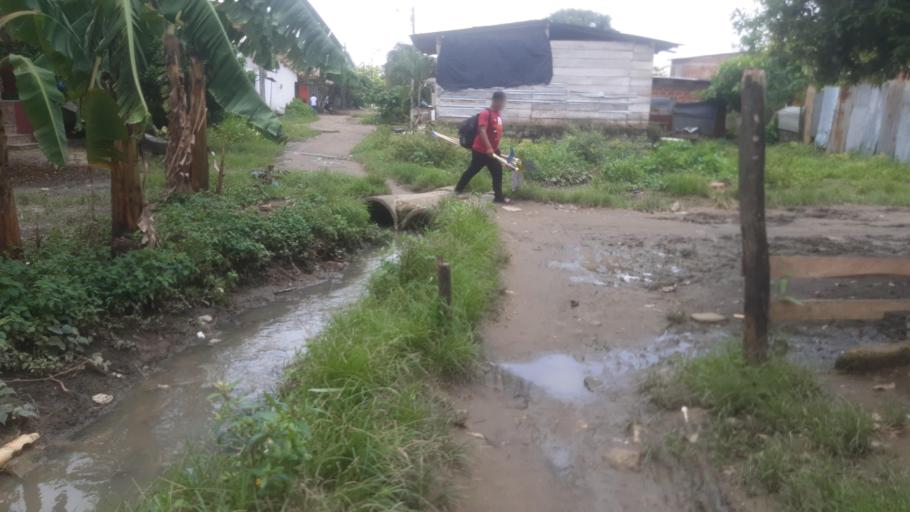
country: CO
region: Antioquia
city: Apartado
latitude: 7.9974
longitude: -76.6313
